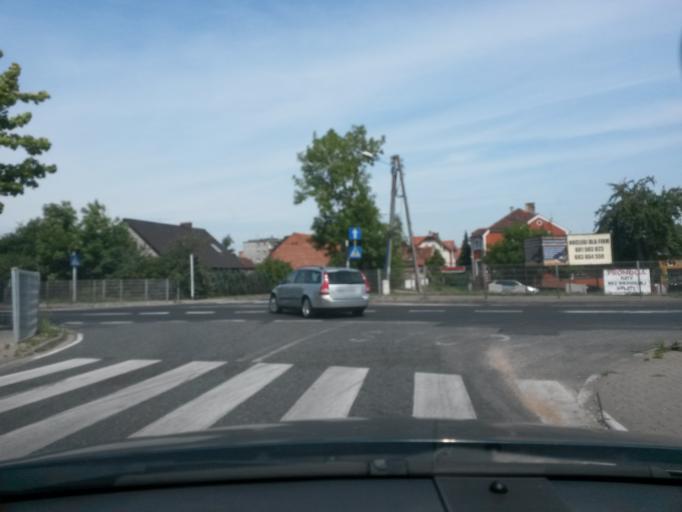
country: PL
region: Lower Silesian Voivodeship
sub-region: Powiat legnicki
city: Prochowice
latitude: 51.2706
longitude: 16.3638
